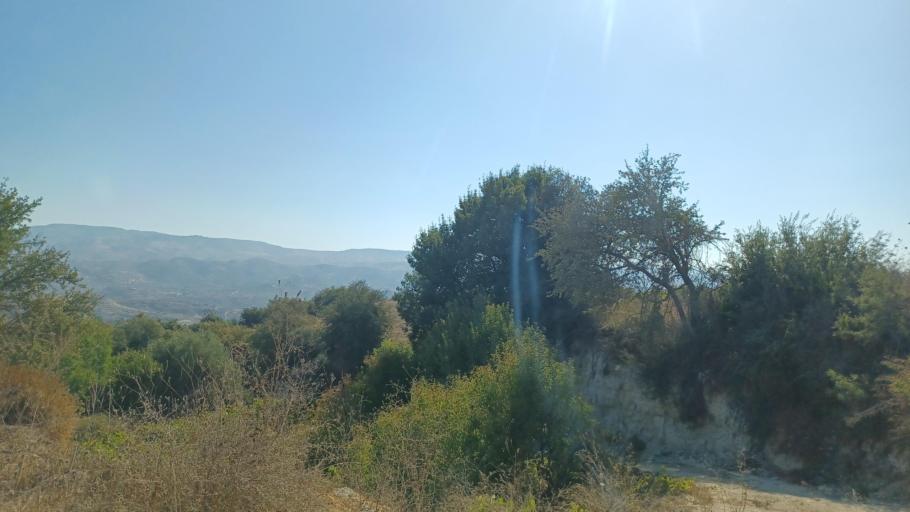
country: CY
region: Pafos
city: Mesogi
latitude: 34.8628
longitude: 32.5154
